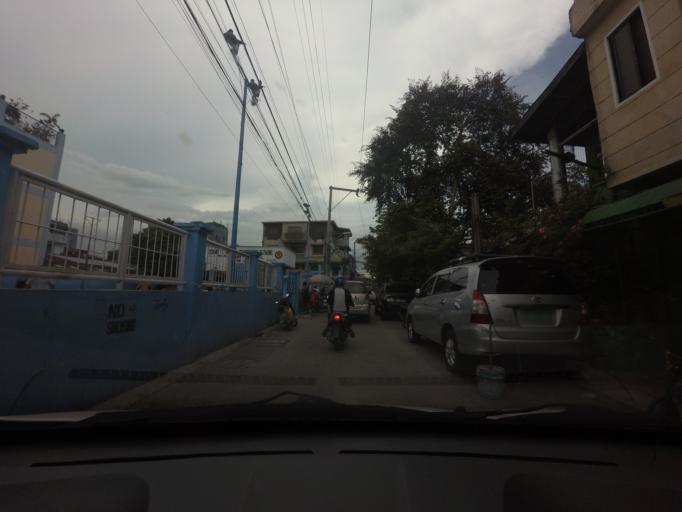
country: PH
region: Calabarzon
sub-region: Province of Rizal
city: Pateros
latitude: 14.5409
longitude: 121.0611
